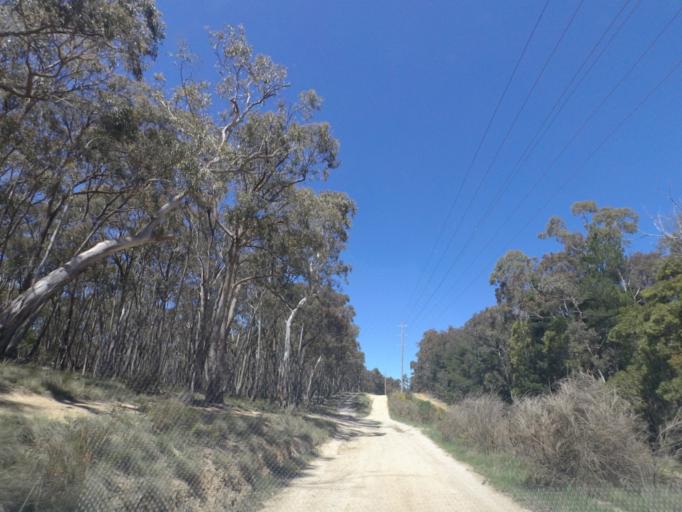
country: AU
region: Victoria
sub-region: Hume
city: Sunbury
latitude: -37.4013
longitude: 144.5613
